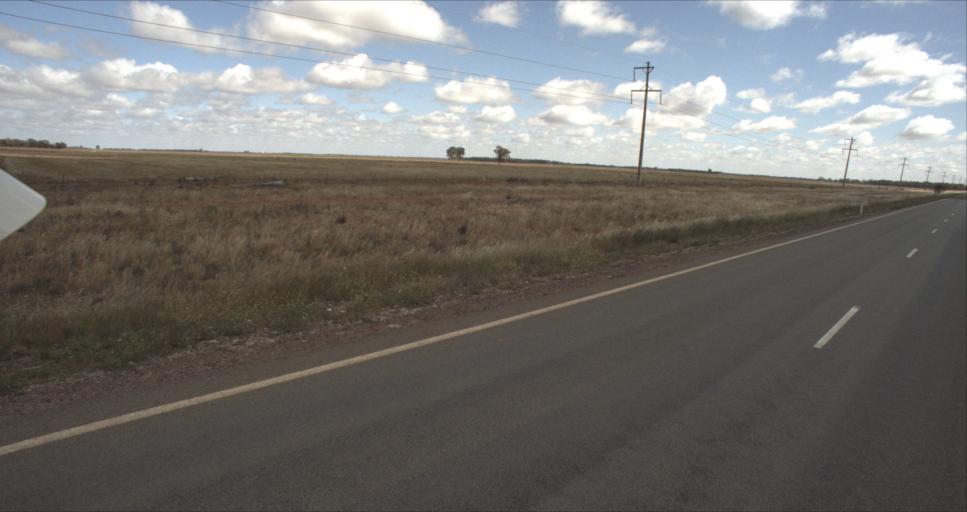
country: AU
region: New South Wales
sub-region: Murrumbidgee Shire
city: Darlington Point
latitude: -34.5915
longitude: 146.1635
